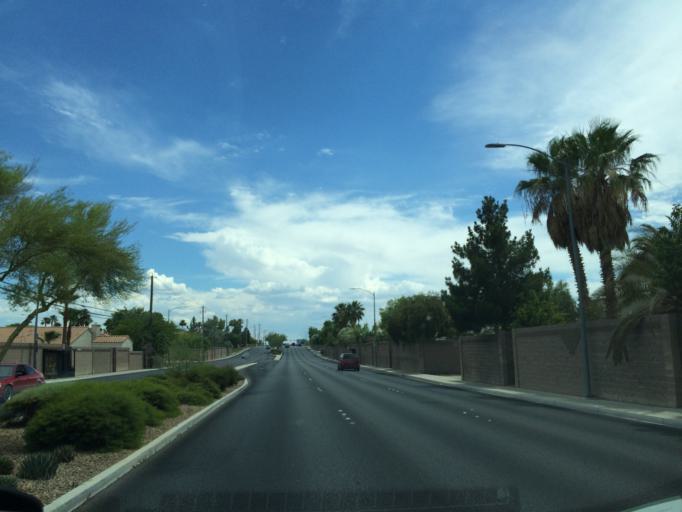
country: US
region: Nevada
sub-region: Clark County
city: North Las Vegas
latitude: 36.2231
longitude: -115.1616
